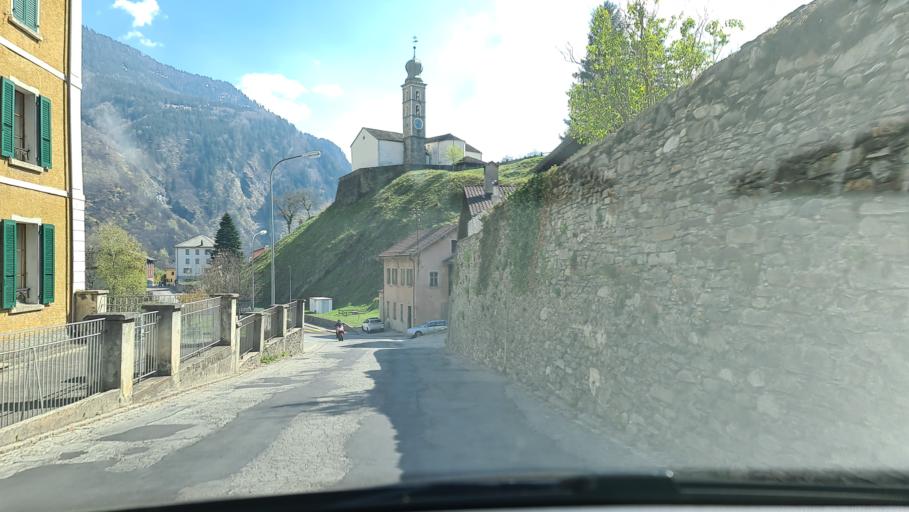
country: CH
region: Grisons
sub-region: Moesa District
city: Mesocco
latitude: 46.3899
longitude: 9.2331
